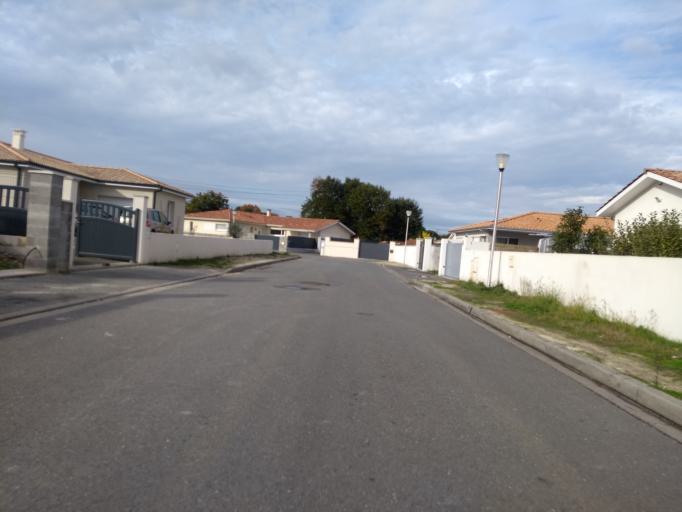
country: FR
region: Aquitaine
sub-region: Departement de la Gironde
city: Cestas
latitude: 44.7376
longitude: -0.6694
